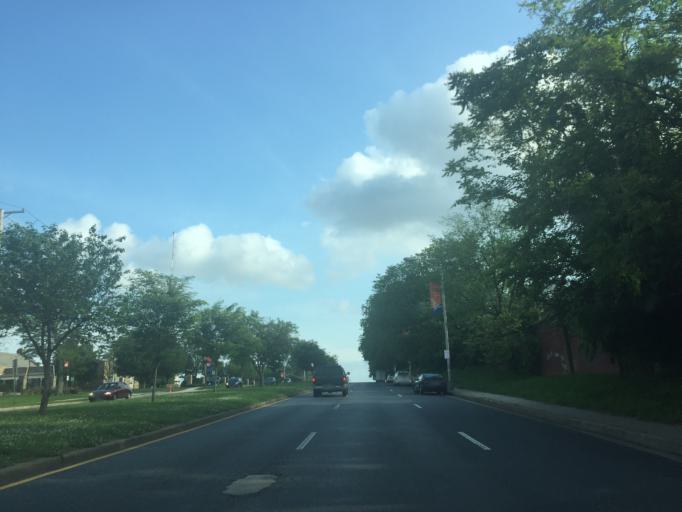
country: US
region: Maryland
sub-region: Baltimore County
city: Parkville
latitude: 39.3443
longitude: -76.5865
